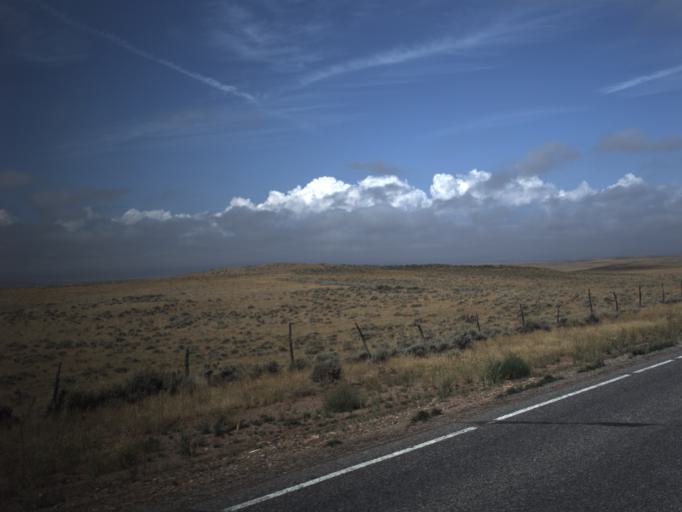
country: US
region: Wyoming
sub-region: Uinta County
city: Evanston
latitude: 41.4229
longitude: -111.0520
